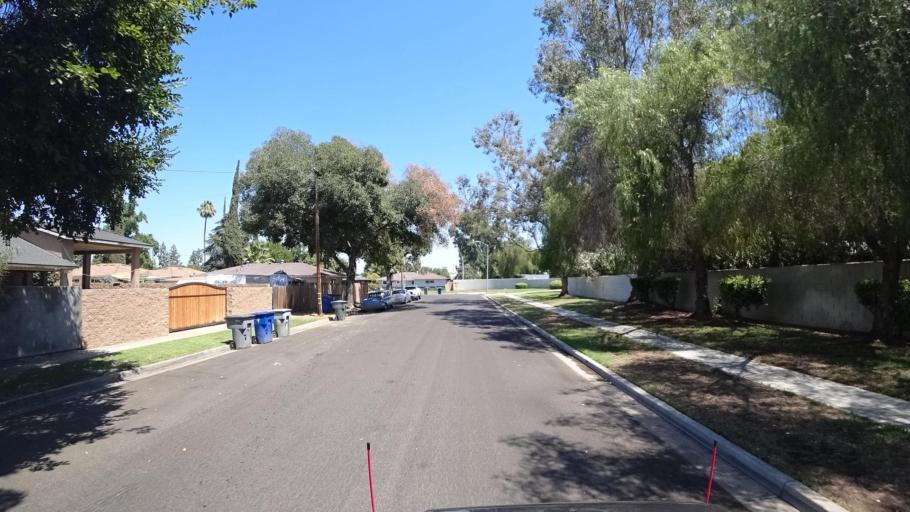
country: US
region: California
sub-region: Fresno County
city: Sunnyside
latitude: 36.7637
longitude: -119.7228
